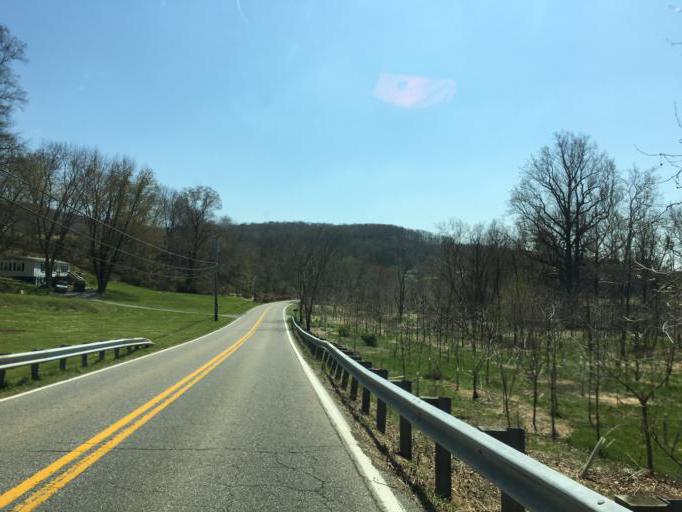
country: US
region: Maryland
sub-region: Frederick County
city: Myersville
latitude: 39.5496
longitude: -77.5261
